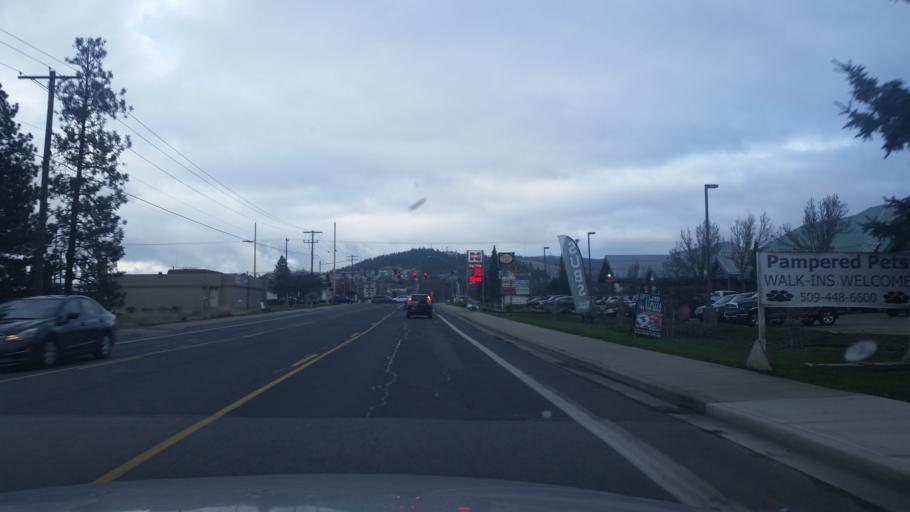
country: US
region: Washington
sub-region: Spokane County
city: Spokane
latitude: 47.6022
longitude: -117.3707
